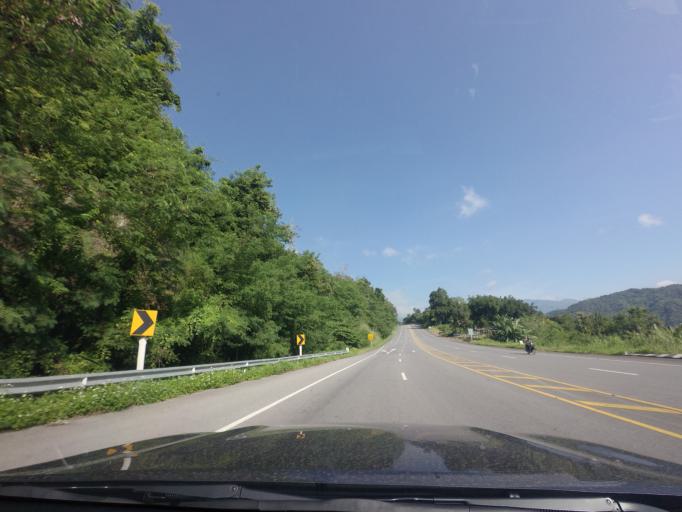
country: TH
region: Phetchabun
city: Khao Kho
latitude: 16.7798
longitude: 101.0926
